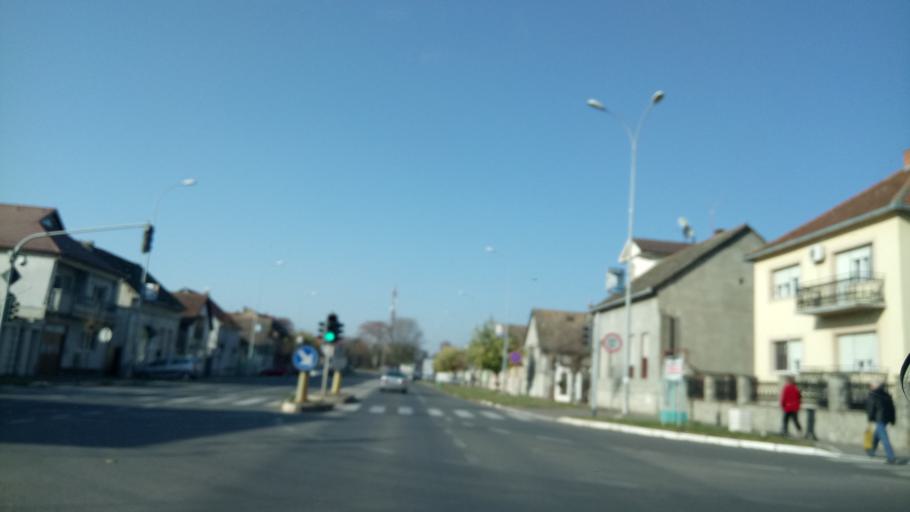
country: RS
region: Autonomna Pokrajina Vojvodina
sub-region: Sremski Okrug
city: Ingija
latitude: 45.0509
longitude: 20.0775
